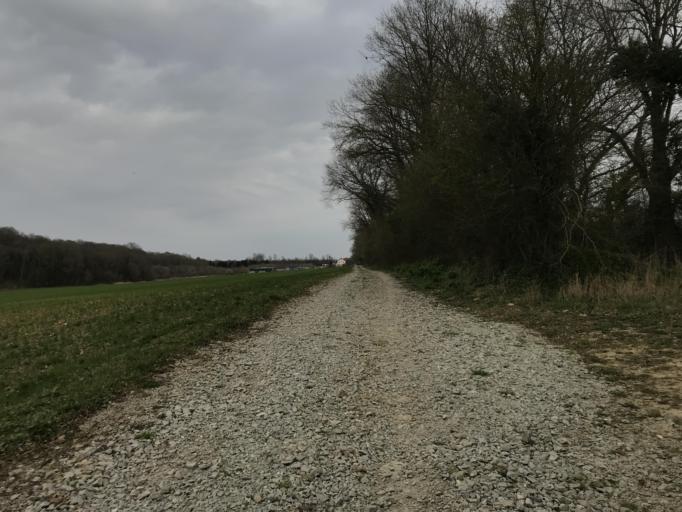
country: FR
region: Ile-de-France
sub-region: Departement de l'Essonne
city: Limours
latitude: 48.6484
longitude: 2.0519
